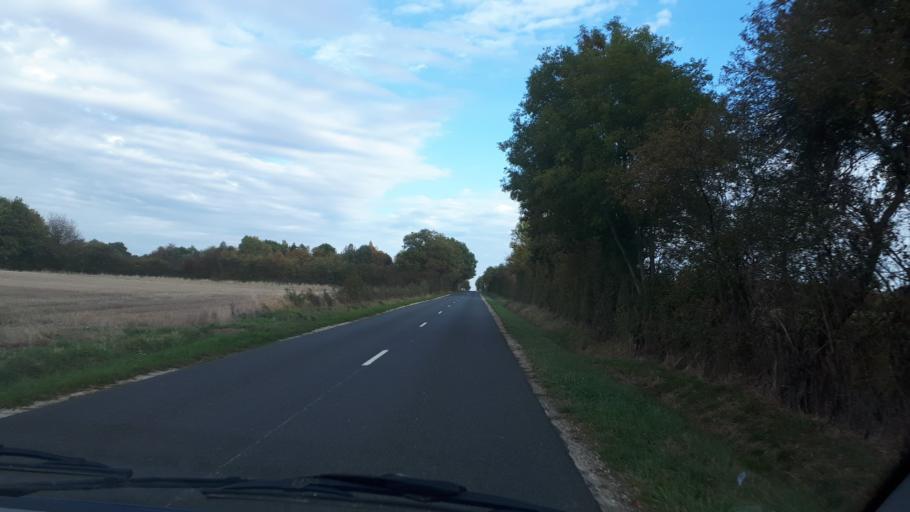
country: FR
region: Centre
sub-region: Departement du Loir-et-Cher
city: Mondoubleau
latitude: 47.9393
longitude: 0.9331
